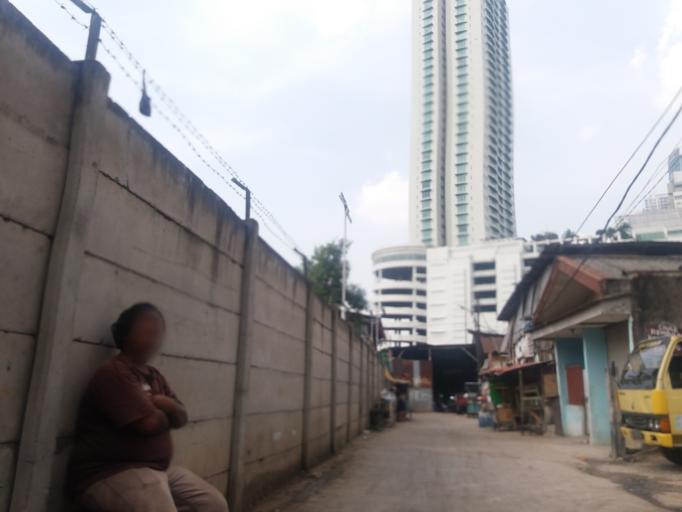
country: ID
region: Jakarta Raya
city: Jakarta
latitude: -6.2230
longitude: 106.8241
